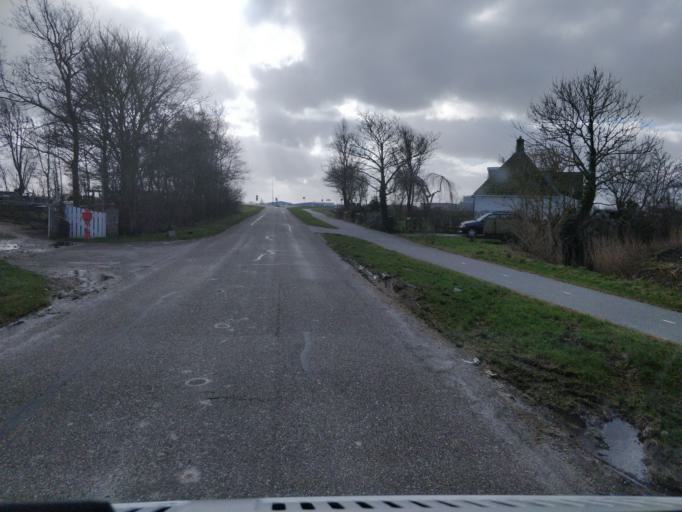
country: NL
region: Friesland
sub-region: Gemeente Harlingen
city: Harlingen
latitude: 53.1835
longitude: 5.4393
